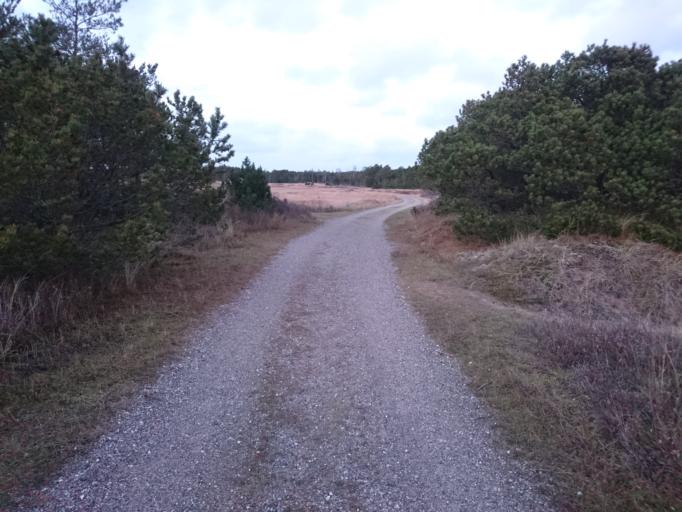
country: DK
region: North Denmark
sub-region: Frederikshavn Kommune
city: Skagen
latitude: 57.7081
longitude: 10.5474
